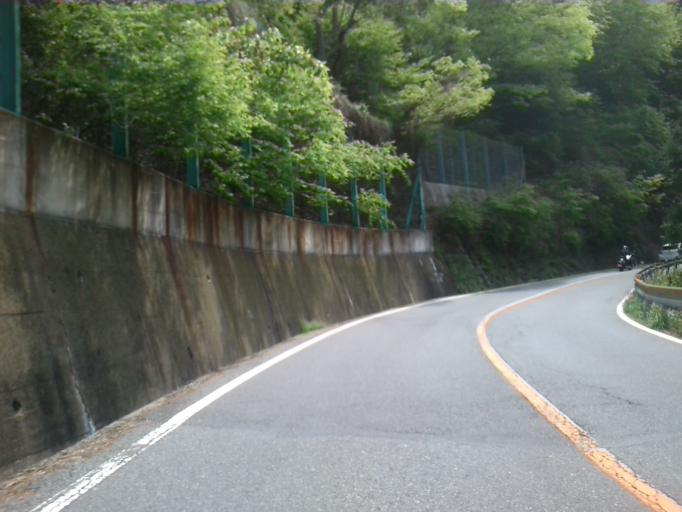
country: JP
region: Kyoto
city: Kameoka
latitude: 34.9851
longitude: 135.5333
